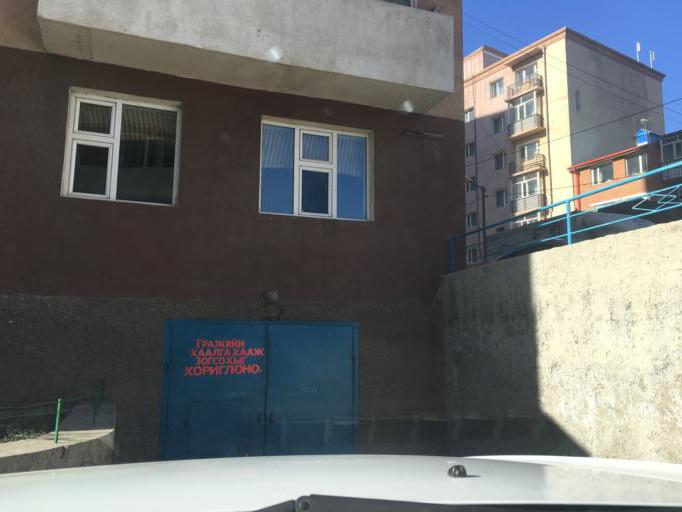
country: MN
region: Ulaanbaatar
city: Ulaanbaatar
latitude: 47.9206
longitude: 106.8579
